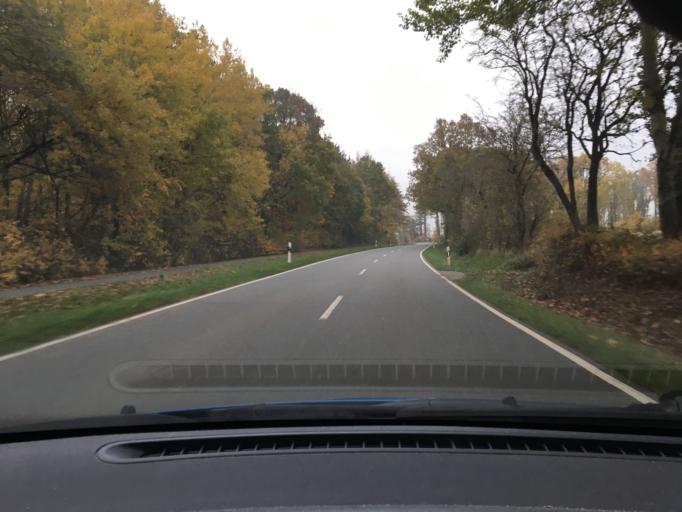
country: DE
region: Schleswig-Holstein
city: Husum
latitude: 54.5110
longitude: 9.0540
